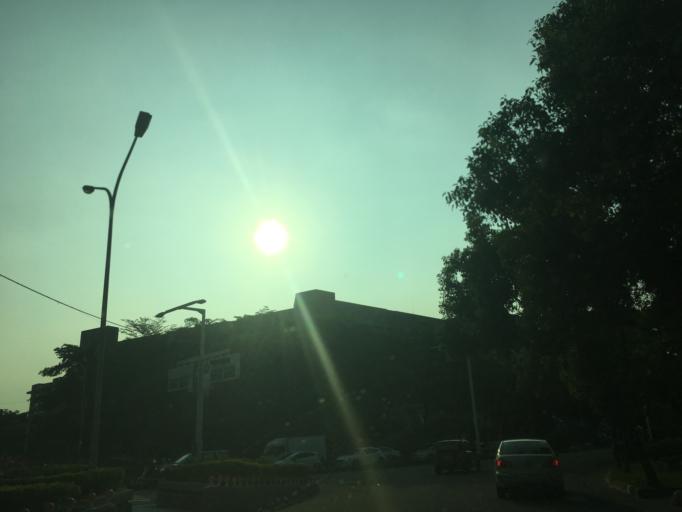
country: TW
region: Taiwan
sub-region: Taichung City
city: Taichung
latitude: 24.1266
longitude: 120.6704
